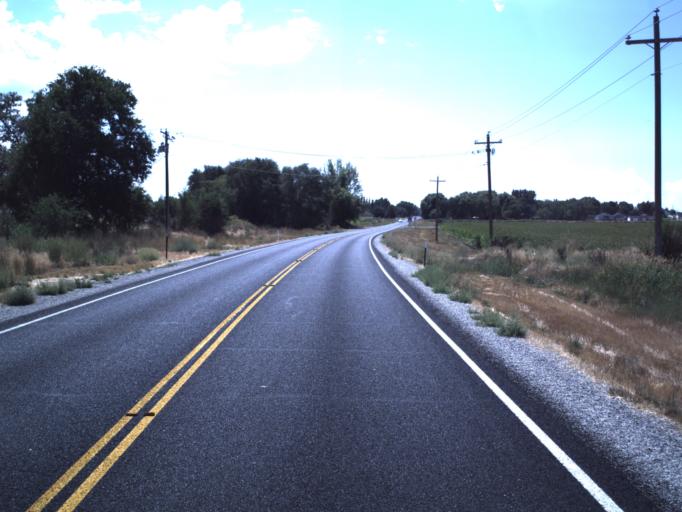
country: US
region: Utah
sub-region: Box Elder County
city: Honeyville
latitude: 41.6280
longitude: -112.1269
